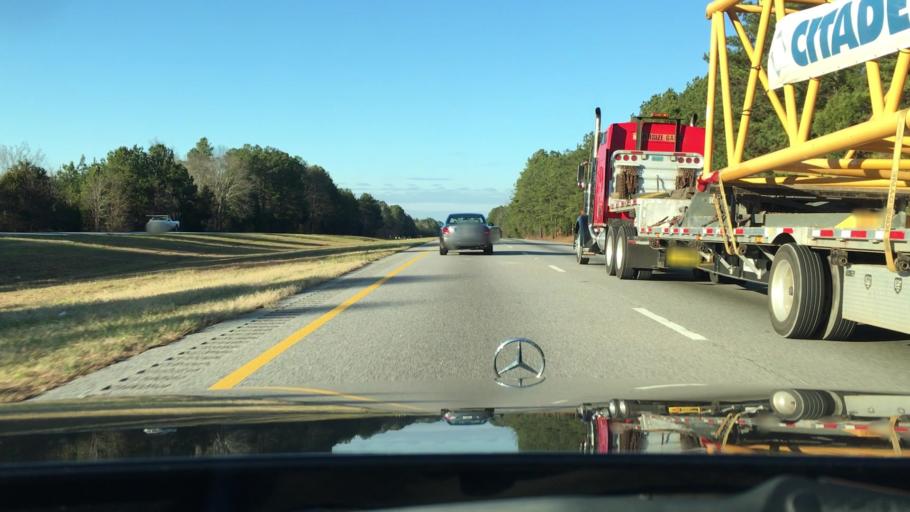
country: US
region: South Carolina
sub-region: Chester County
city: Great Falls
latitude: 34.6804
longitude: -81.0292
